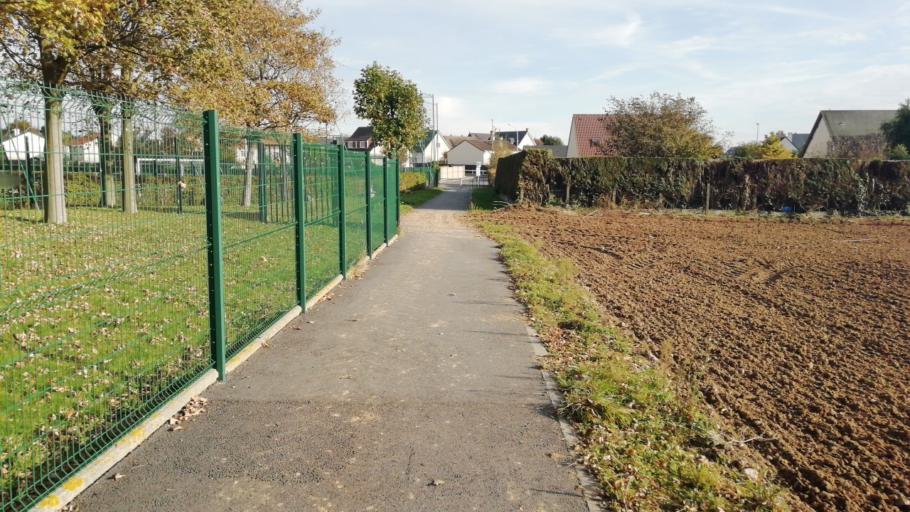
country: FR
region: Haute-Normandie
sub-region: Departement de la Seine-Maritime
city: Rogerville
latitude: 49.5068
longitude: 0.2632
